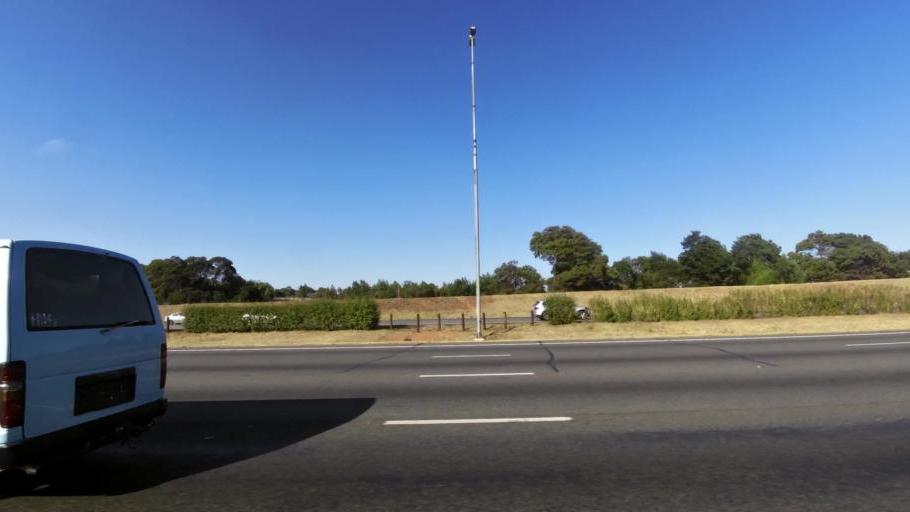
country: ZA
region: Gauteng
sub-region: City of Johannesburg Metropolitan Municipality
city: Johannesburg
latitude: -26.2627
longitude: 27.9790
